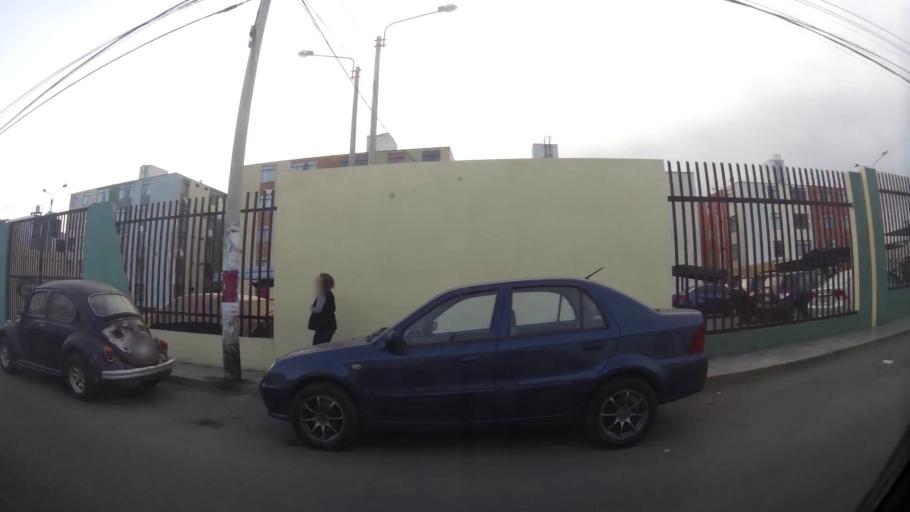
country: PE
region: La Libertad
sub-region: Provincia de Trujillo
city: Trujillo
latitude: -8.0981
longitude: -79.0398
